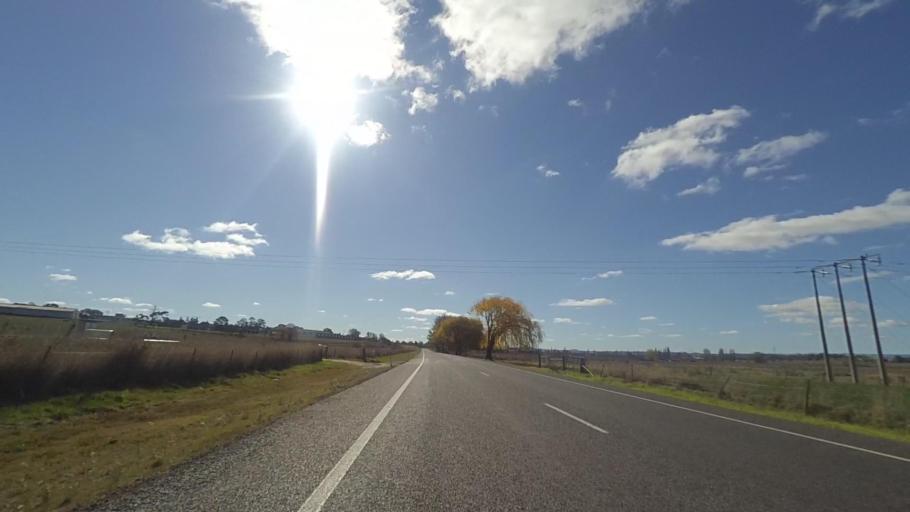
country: AU
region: New South Wales
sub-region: Bathurst Regional
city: Bathurst
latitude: -33.4478
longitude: 149.5789
